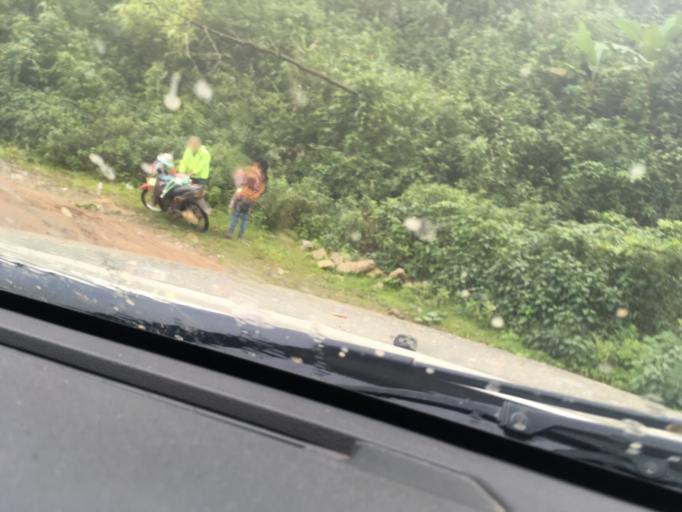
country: LA
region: Phongsali
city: Phongsali
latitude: 21.3981
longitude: 102.1903
